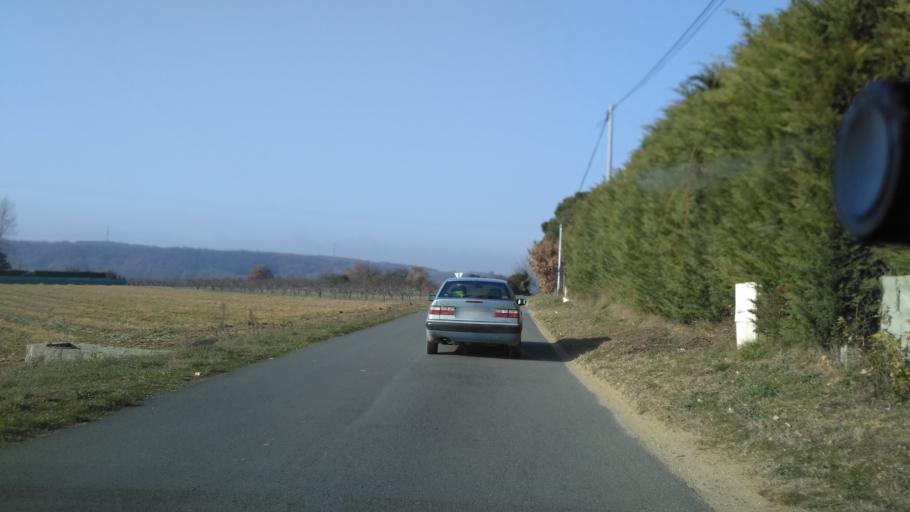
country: FR
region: Rhone-Alpes
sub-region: Departement de la Drome
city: Clerieux
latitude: 45.0578
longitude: 4.9685
